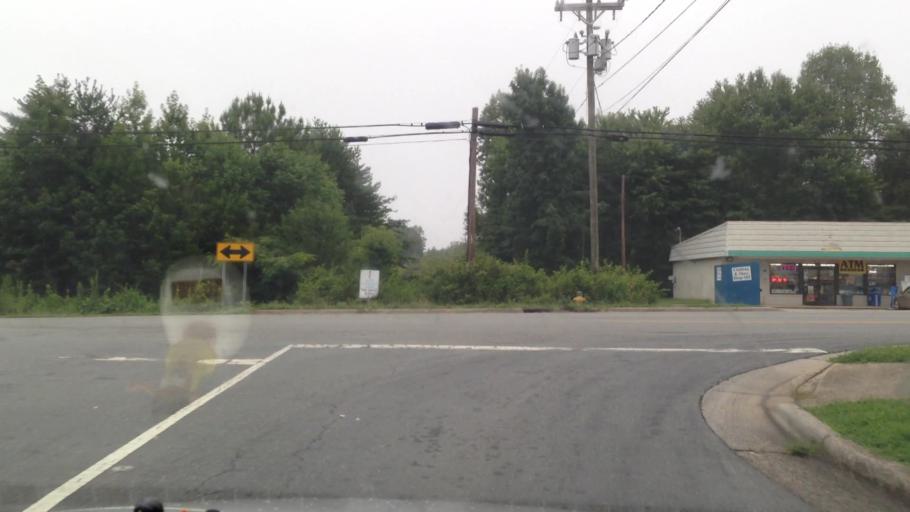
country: US
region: North Carolina
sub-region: Forsyth County
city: Kernersville
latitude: 36.1386
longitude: -80.0697
